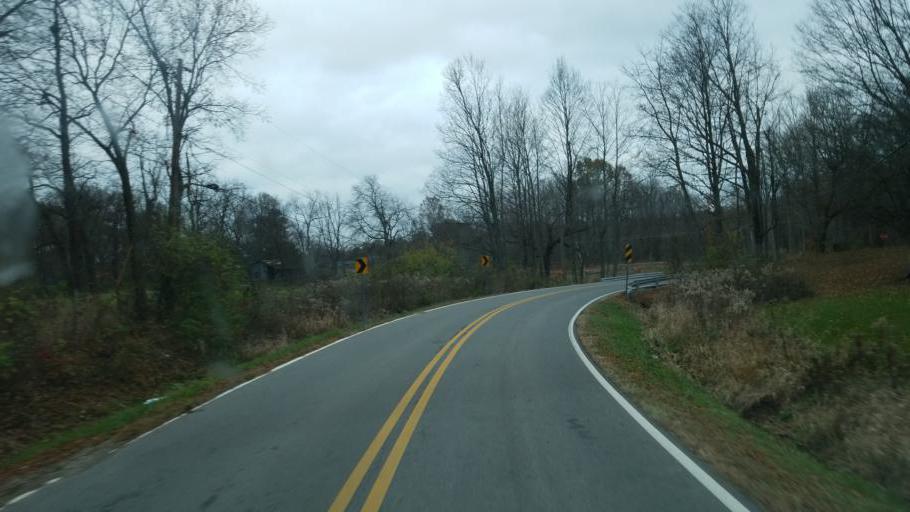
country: US
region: Ohio
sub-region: Delaware County
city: Sunbury
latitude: 40.1872
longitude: -82.8537
